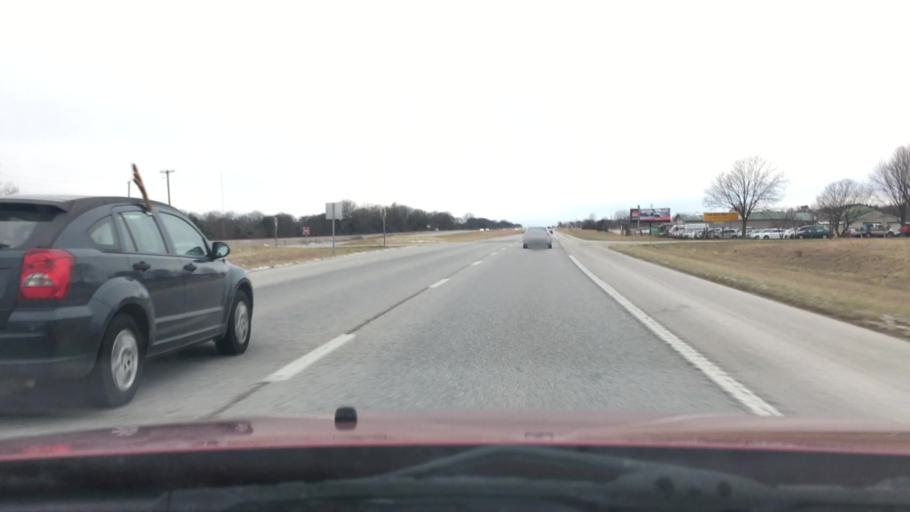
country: US
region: Missouri
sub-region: Webster County
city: Seymour
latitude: 37.1695
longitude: -92.8259
